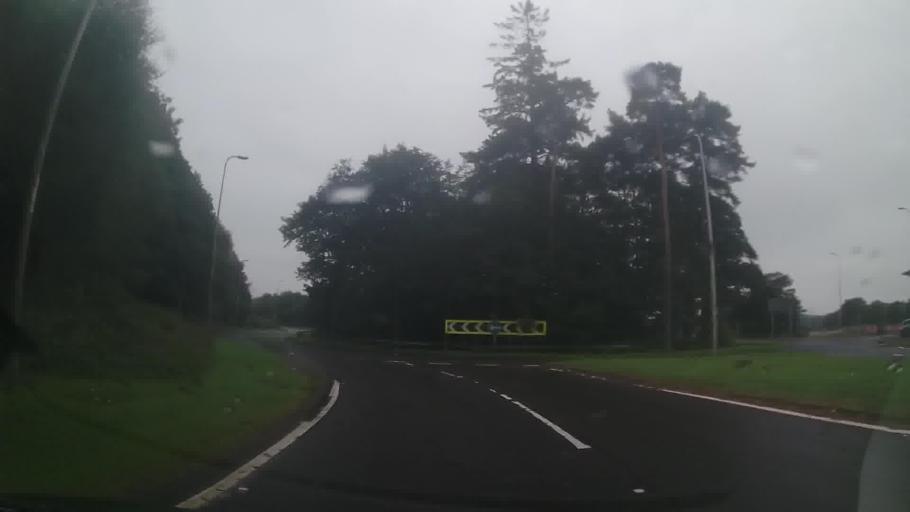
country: GB
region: Scotland
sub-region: North Ayrshire
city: Fairlie
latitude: 55.7286
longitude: -4.8657
